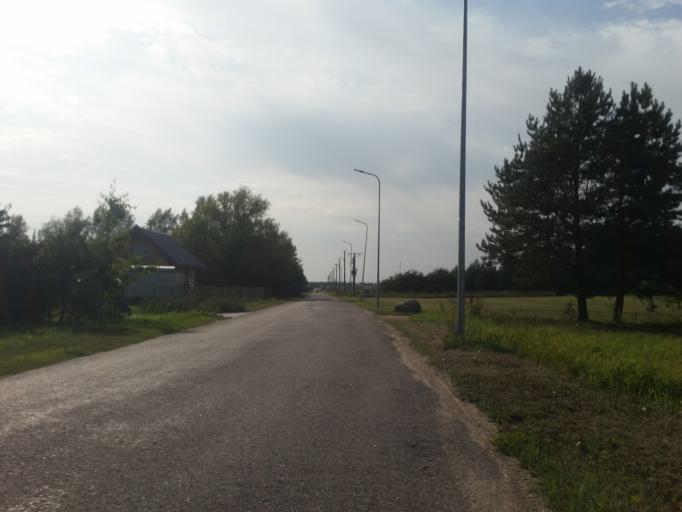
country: LV
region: Ikskile
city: Ikskile
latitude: 56.8189
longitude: 24.5288
